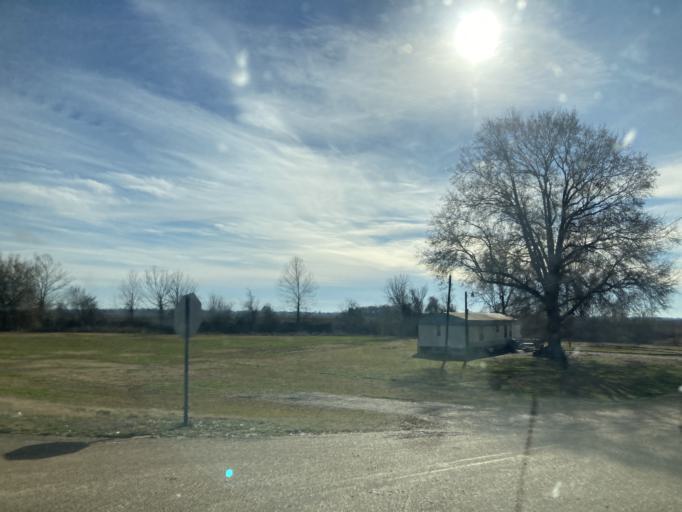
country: US
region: Mississippi
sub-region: Humphreys County
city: Belzoni
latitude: 32.9955
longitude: -90.6226
